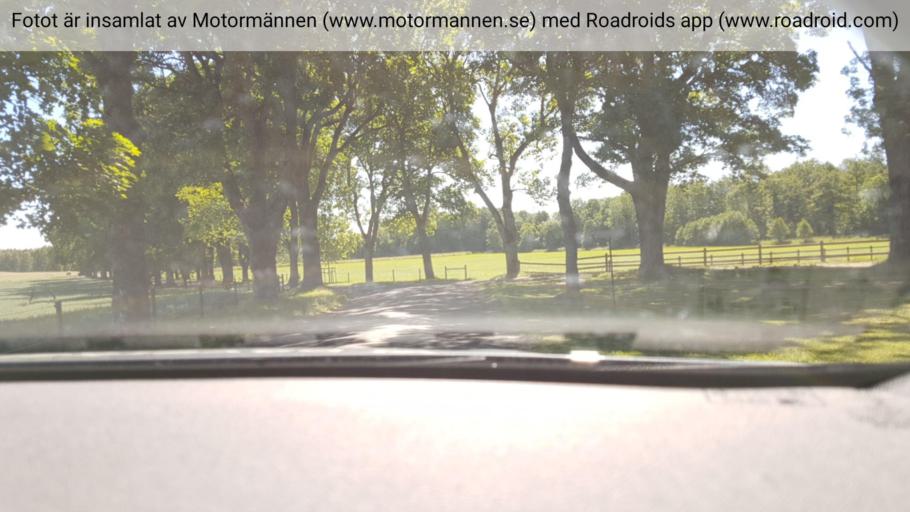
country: SE
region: Vaestra Goetaland
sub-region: Tidaholms Kommun
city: Tidaholm
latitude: 58.1956
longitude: 13.8212
